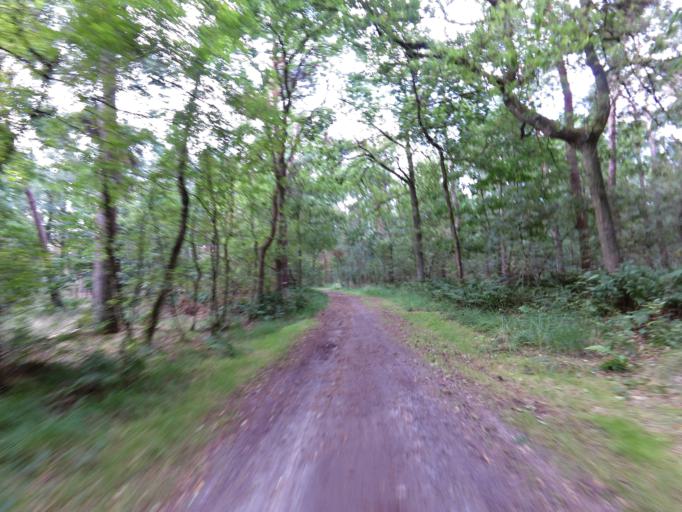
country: NL
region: North Brabant
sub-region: Gemeente Best
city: Best
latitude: 51.5152
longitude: 5.4245
